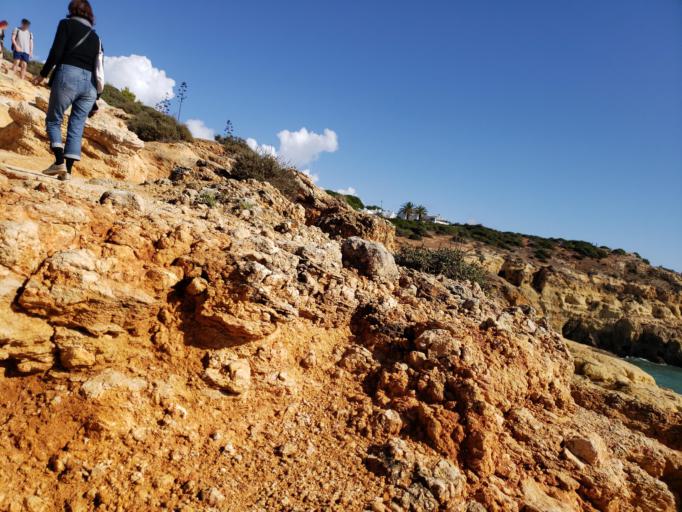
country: PT
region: Faro
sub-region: Lagoa
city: Carvoeiro
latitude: 37.0928
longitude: -8.4649
